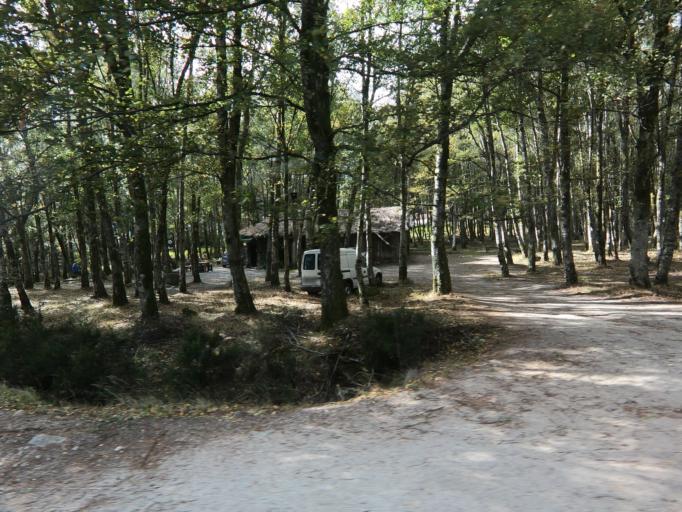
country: PT
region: Vila Real
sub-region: Vila Real
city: Vila Real
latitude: 41.3486
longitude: -7.7904
